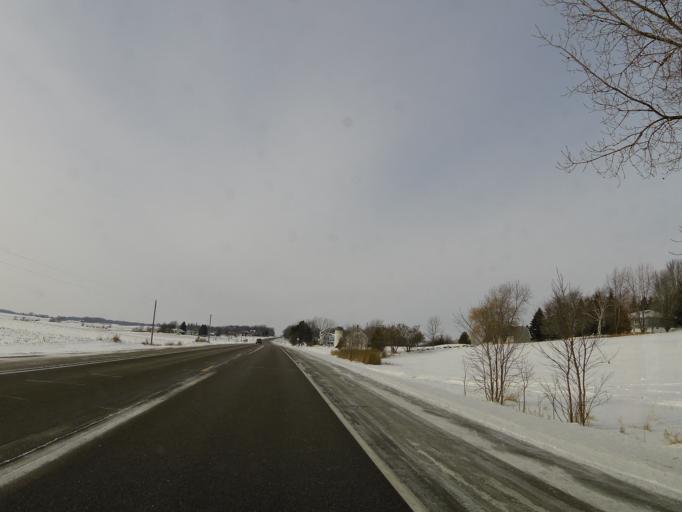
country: US
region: Minnesota
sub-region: Hennepin County
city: Saint Bonifacius
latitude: 44.9054
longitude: -93.7920
